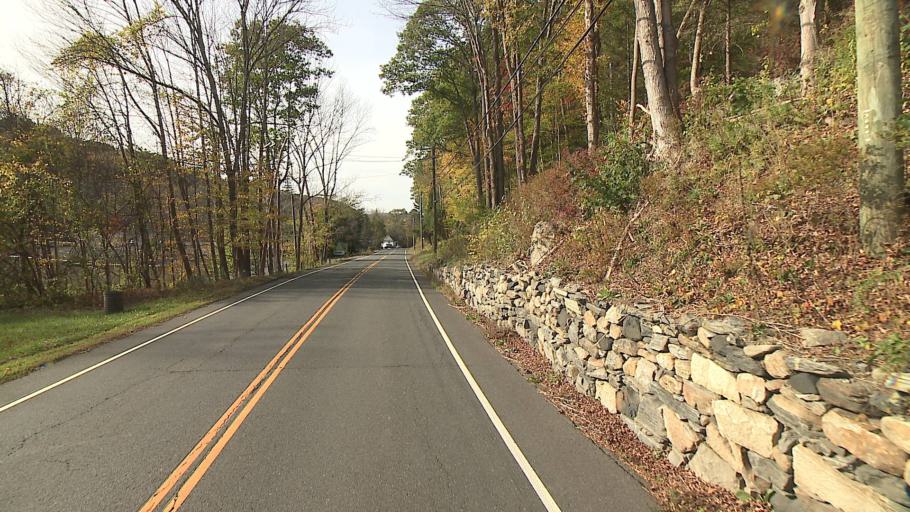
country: US
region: Connecticut
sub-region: Litchfield County
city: Winchester Center
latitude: 41.9960
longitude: -73.2090
